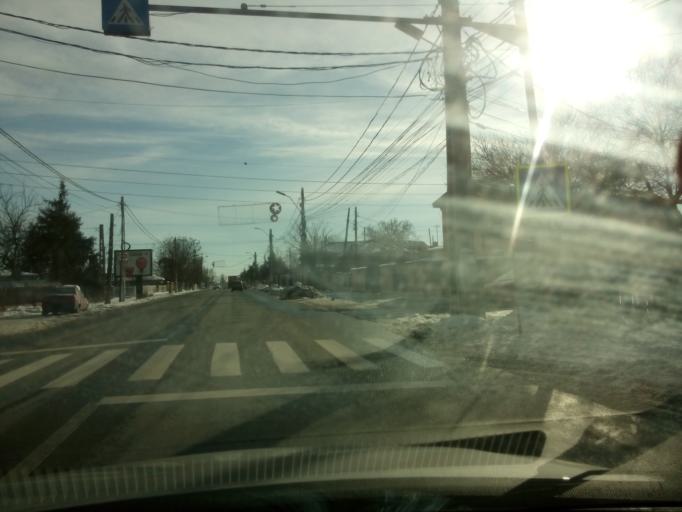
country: RO
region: Ilfov
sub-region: Comuna Popesti-Leordeni
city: Popesti-Leordeni
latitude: 44.3744
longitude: 26.1771
